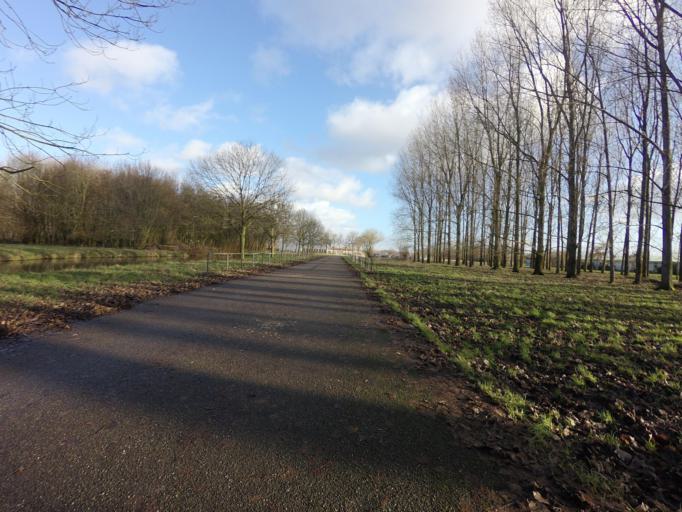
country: NL
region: Utrecht
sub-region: Gemeente Nieuwegein
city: Nieuwegein
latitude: 52.0592
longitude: 5.0742
